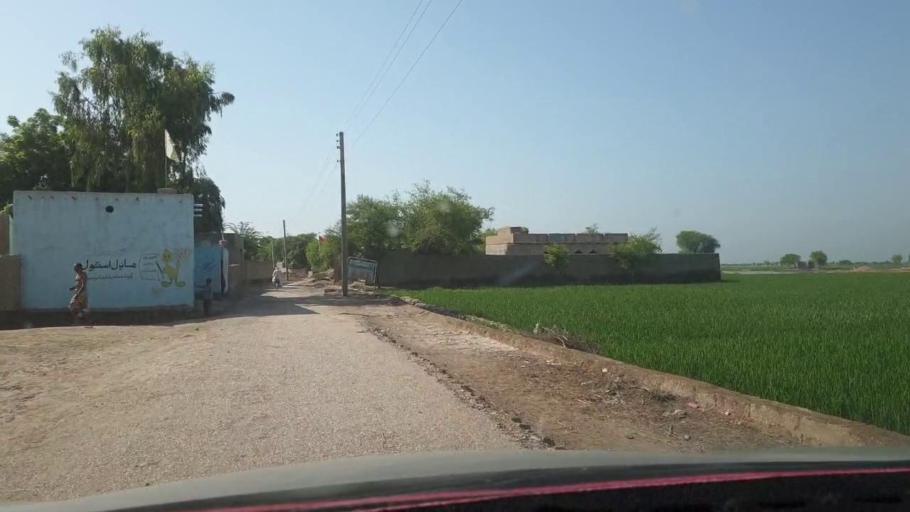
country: PK
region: Sindh
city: Nasirabad
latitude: 27.3836
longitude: 67.8781
